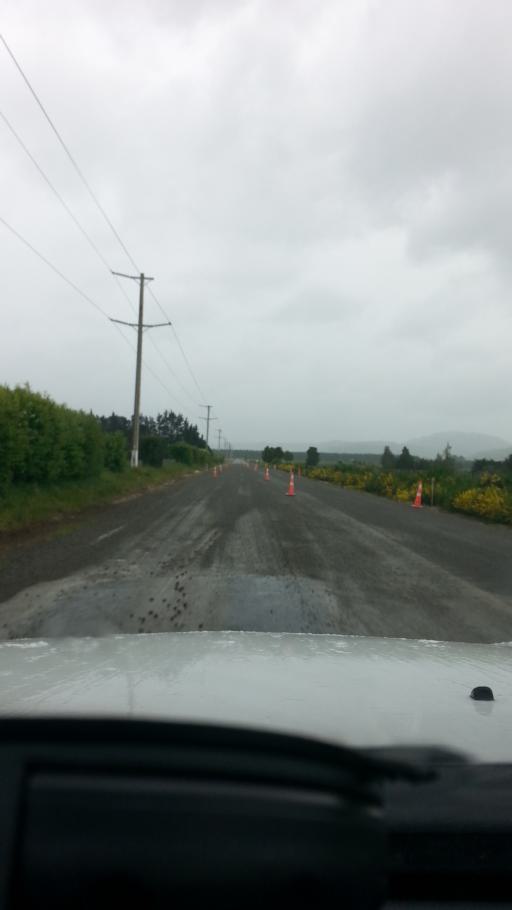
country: NZ
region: Wellington
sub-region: Masterton District
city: Masterton
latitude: -40.8241
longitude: 175.6245
